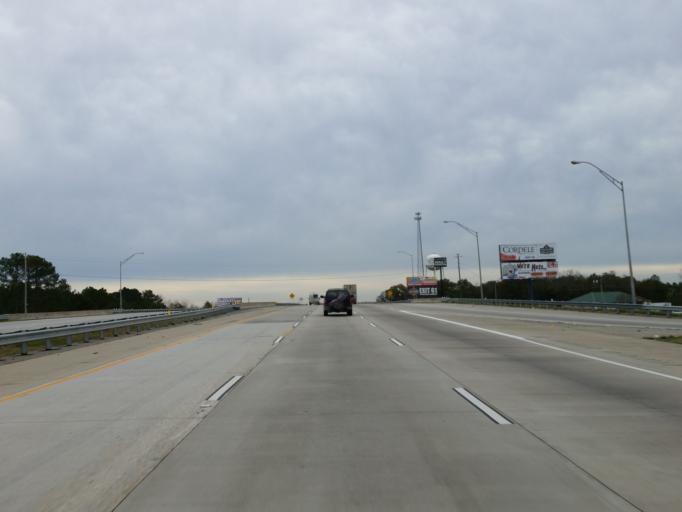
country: US
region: Georgia
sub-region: Dooly County
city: Unadilla
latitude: 32.2482
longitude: -83.7440
